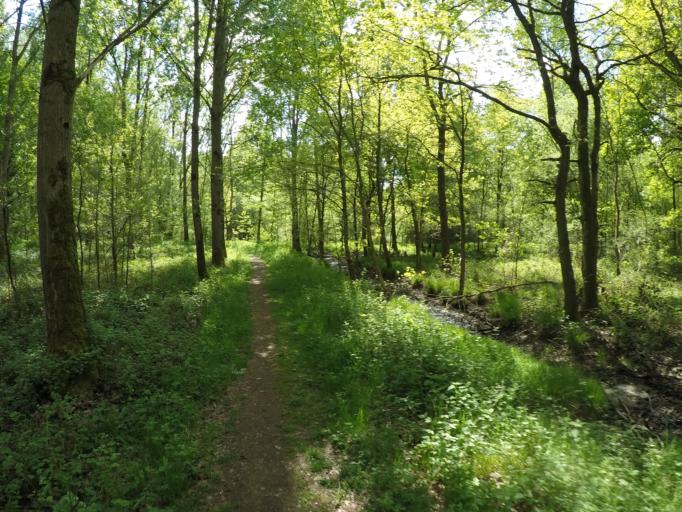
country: BE
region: Flanders
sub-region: Provincie Antwerpen
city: Lier
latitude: 51.1323
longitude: 4.6089
